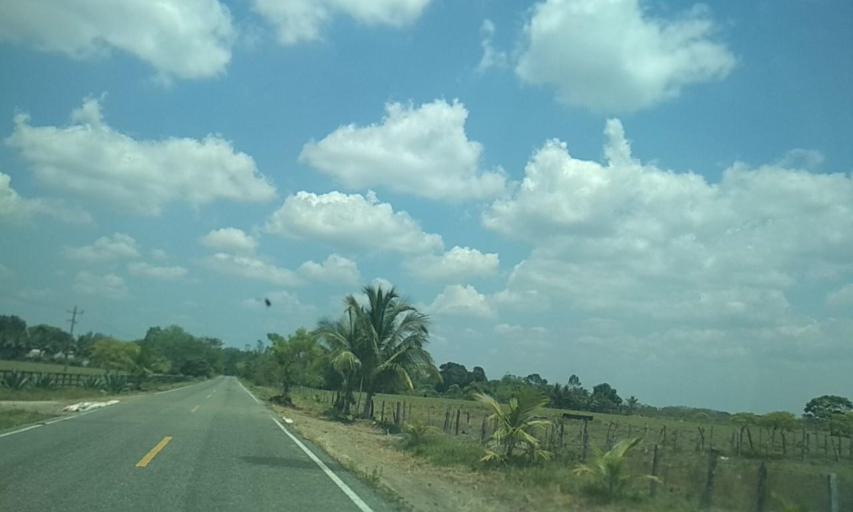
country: MX
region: Tabasco
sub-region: Huimanguillo
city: Huapacal 1ra. Seccion
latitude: 17.7529
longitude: -93.7329
